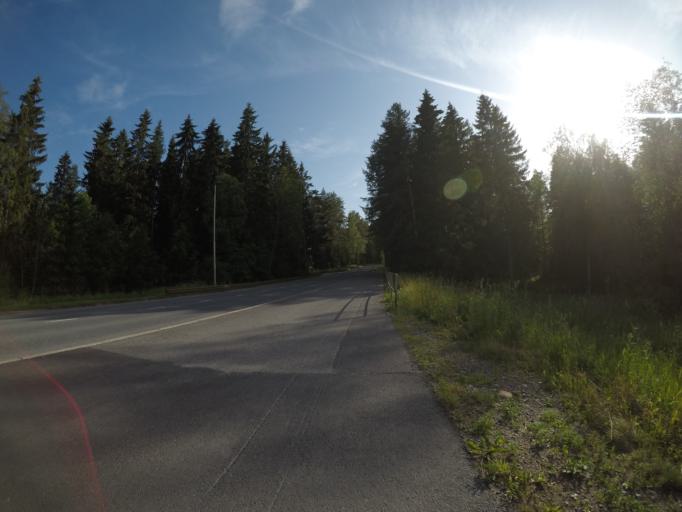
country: FI
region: Haeme
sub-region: Haemeenlinna
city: Haemeenlinna
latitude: 60.9766
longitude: 24.3988
